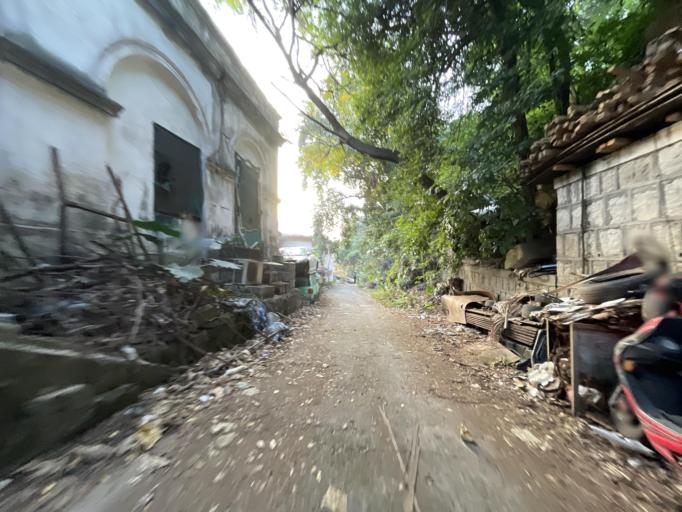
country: CN
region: Guangdong
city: Wanzai
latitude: 22.2107
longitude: 113.5375
